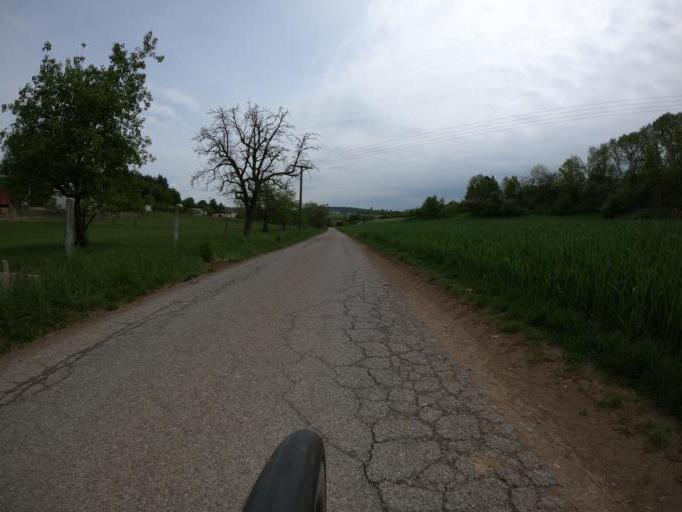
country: DE
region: Baden-Wuerttemberg
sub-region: Regierungsbezirk Stuttgart
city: Aidlingen
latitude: 48.6857
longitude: 8.8858
